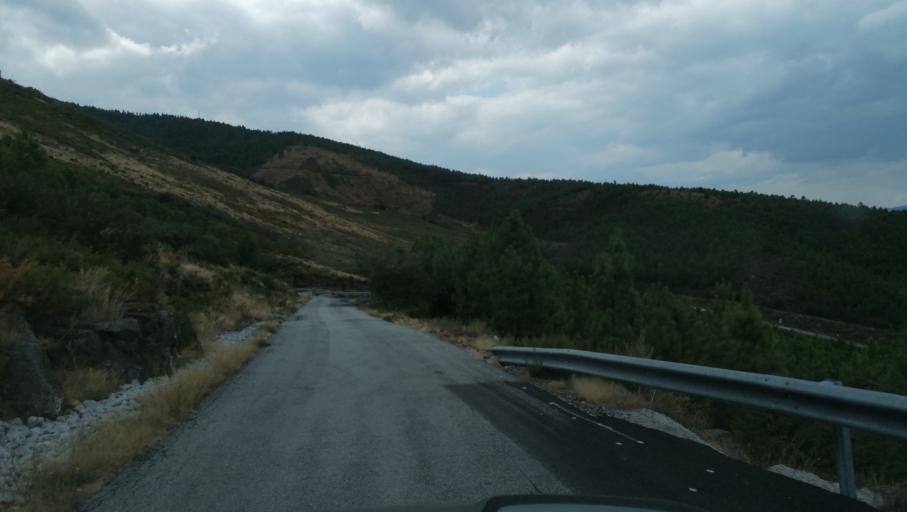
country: PT
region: Vila Real
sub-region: Vila Pouca de Aguiar
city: Vila Pouca de Aguiar
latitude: 41.5548
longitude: -7.7082
